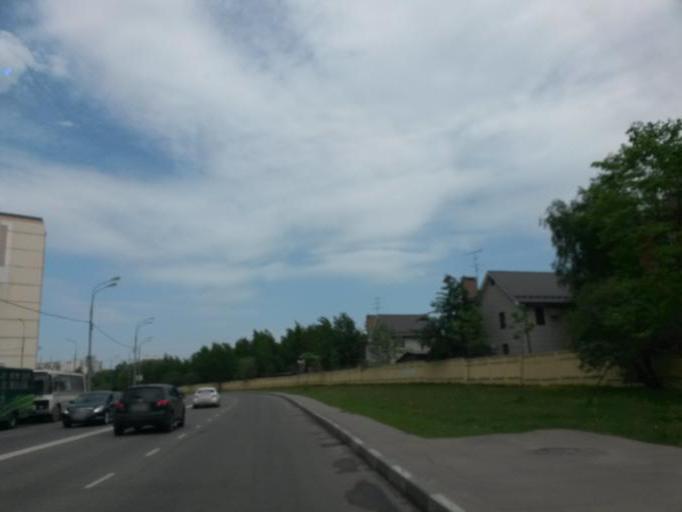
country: RU
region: Moskovskaya
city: Shcherbinka
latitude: 55.5370
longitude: 37.5421
